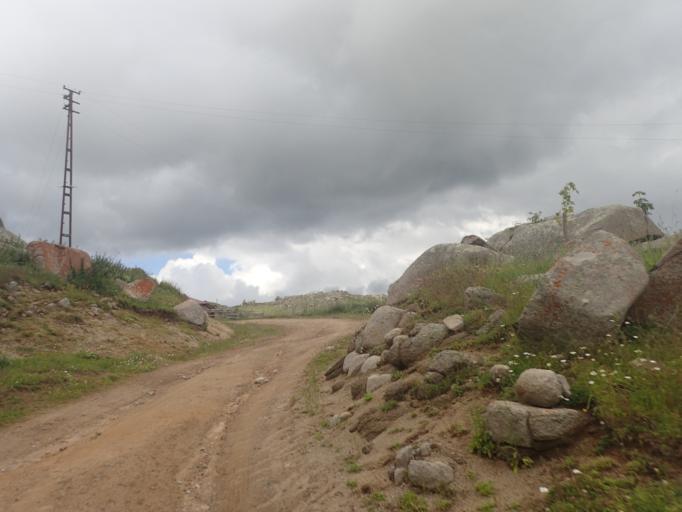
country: TR
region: Ordu
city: Yesilce
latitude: 40.5730
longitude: 37.9611
